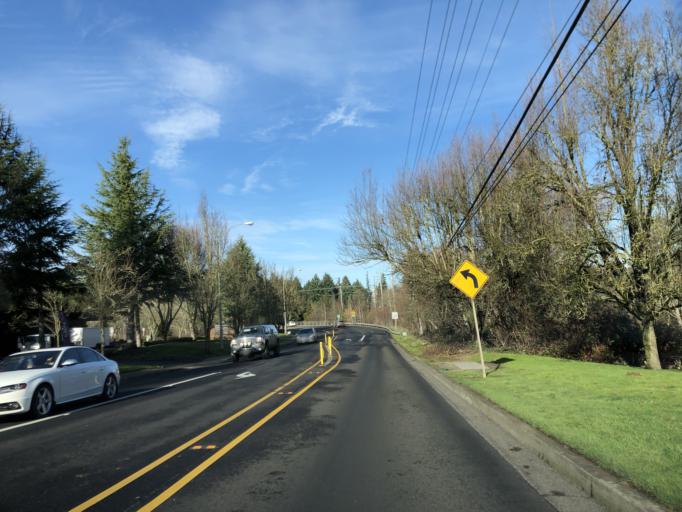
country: US
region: Oregon
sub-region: Washington County
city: Tualatin
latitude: 45.3806
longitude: -122.7439
